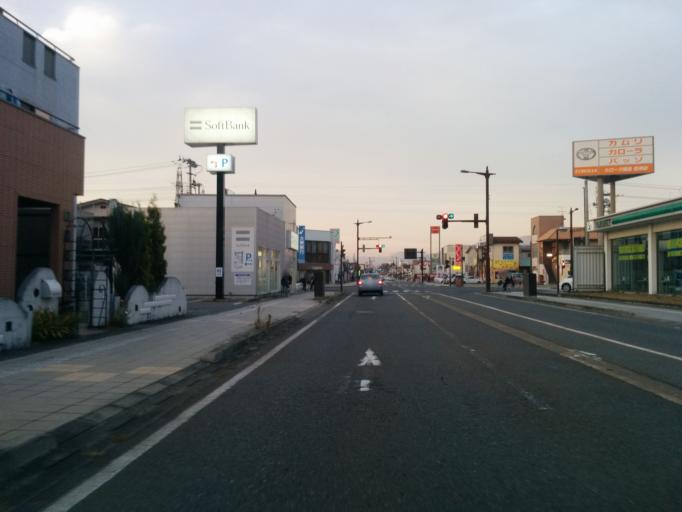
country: JP
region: Fukushima
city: Kitakata
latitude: 37.4779
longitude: 139.9250
